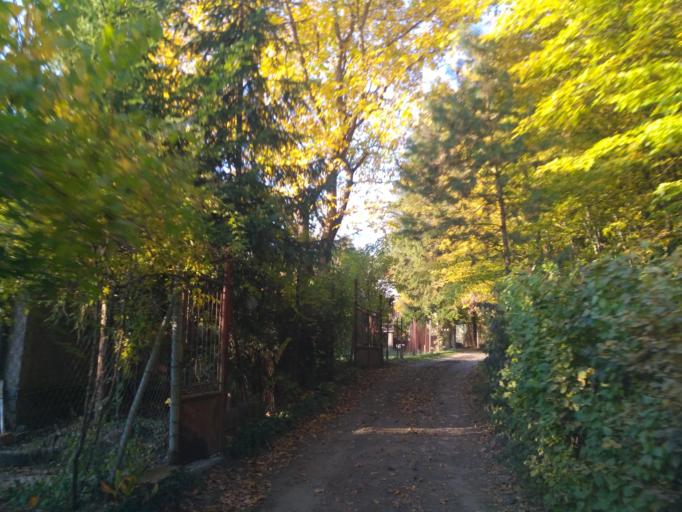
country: SK
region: Kosicky
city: Kosice
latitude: 48.7691
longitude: 21.2905
